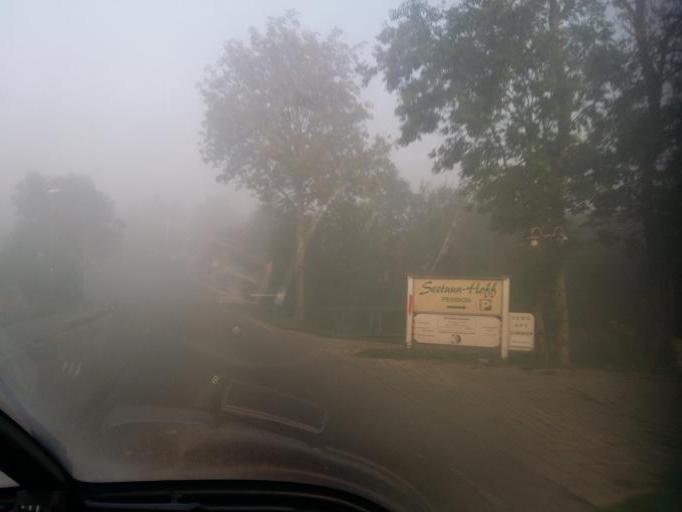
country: DE
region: Schleswig-Holstein
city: Elisabeth-Sophien-Koog
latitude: 54.4923
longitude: 8.8654
